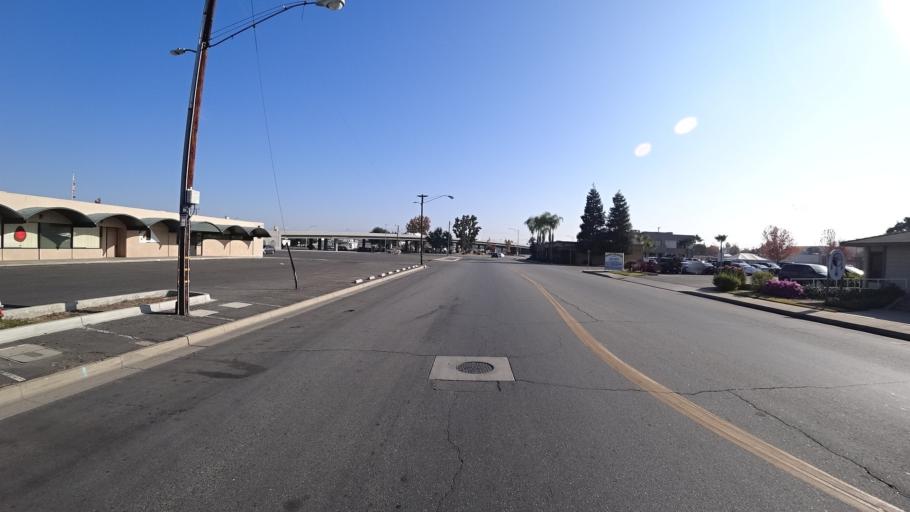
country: US
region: California
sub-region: Kern County
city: Bakersfield
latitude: 35.3868
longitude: -119.0206
